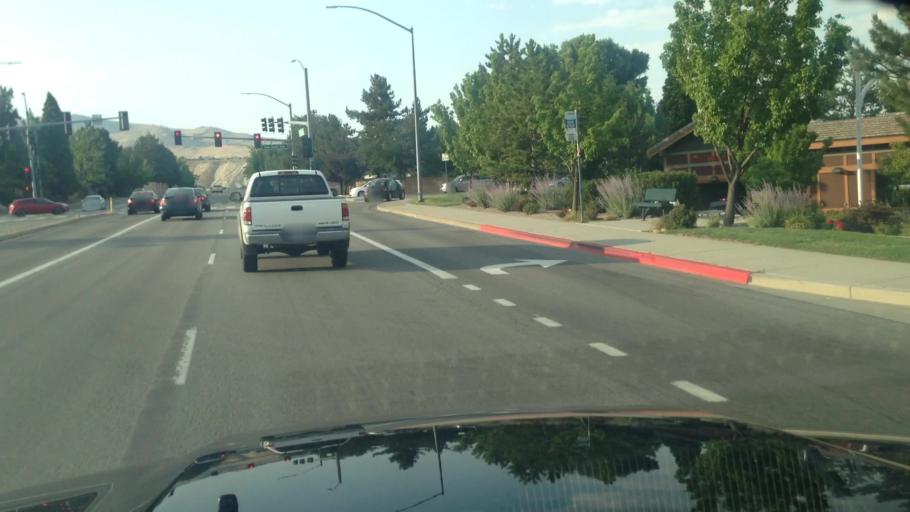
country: US
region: Nevada
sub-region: Washoe County
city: Mogul
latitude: 39.5288
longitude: -119.8820
